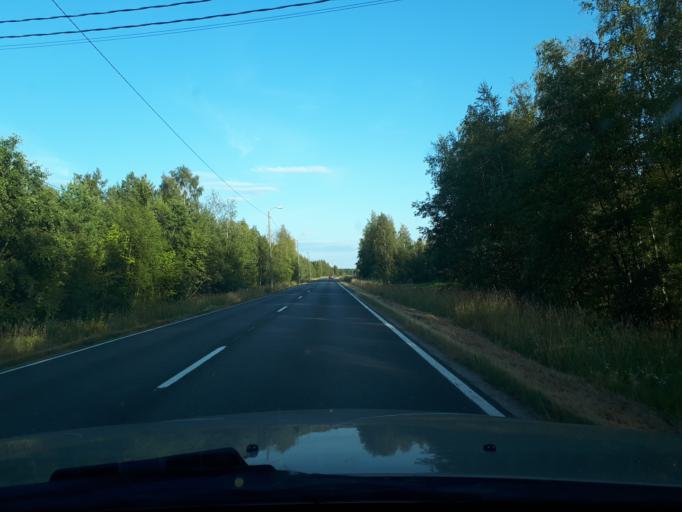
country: FI
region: Northern Ostrobothnia
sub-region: Oulu
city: Oulunsalo
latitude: 64.9847
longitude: 25.2654
